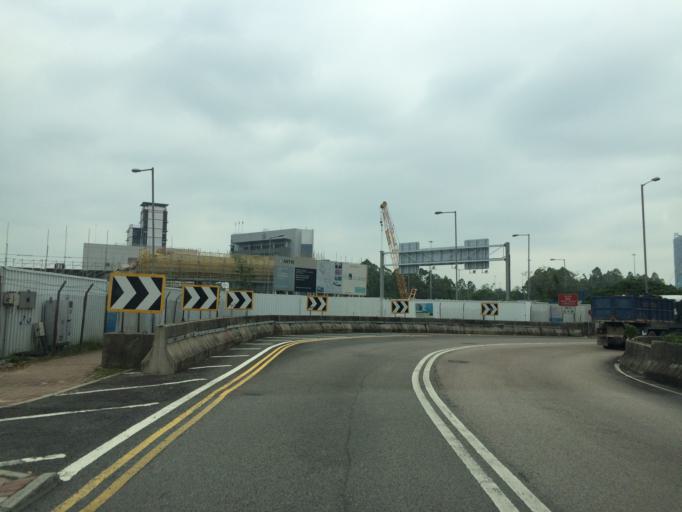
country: HK
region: Kowloon City
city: Kowloon
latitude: 22.3093
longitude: 114.1653
